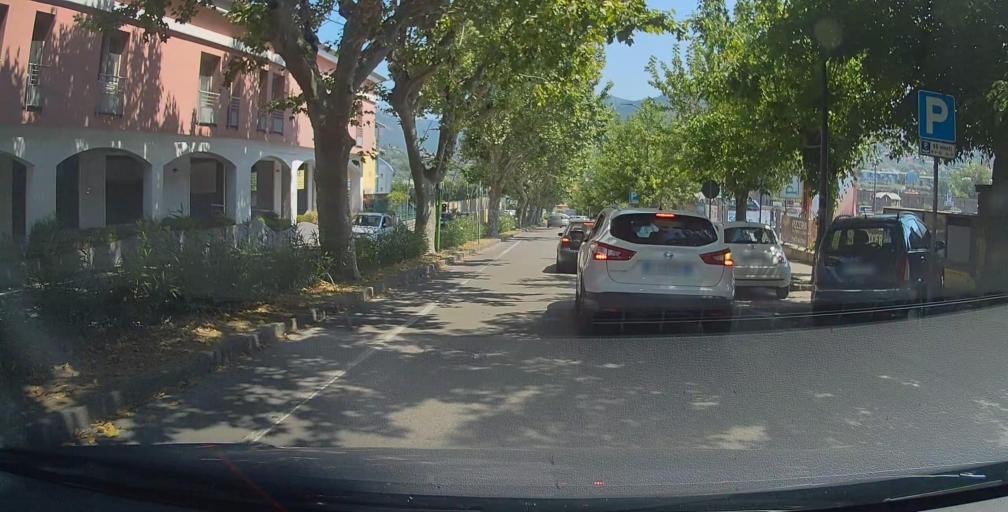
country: IT
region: Campania
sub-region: Provincia di Salerno
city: Cava De Tirreni
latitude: 40.7122
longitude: 14.7015
